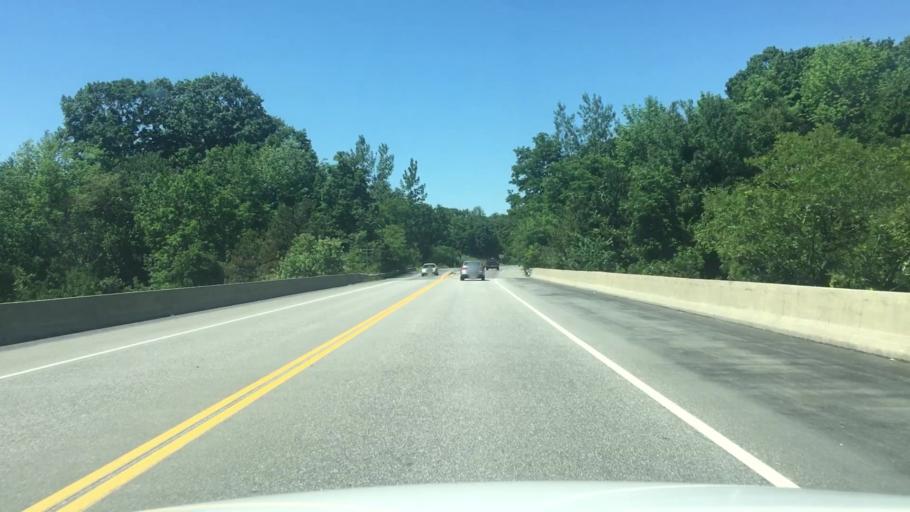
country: US
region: Maine
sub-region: Kennebec County
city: Waterville
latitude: 44.5317
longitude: -69.6479
